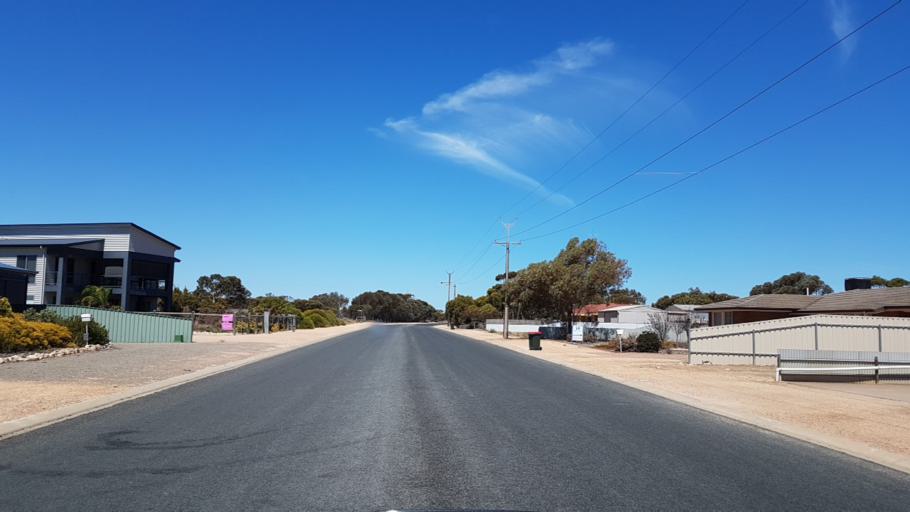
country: AU
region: South Australia
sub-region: Copper Coast
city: Wallaroo
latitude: -34.0522
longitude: 137.5758
